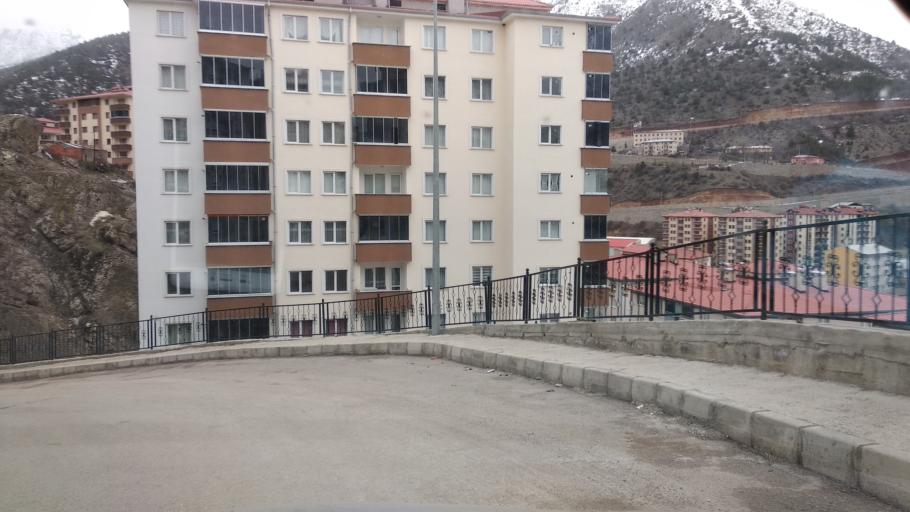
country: TR
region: Gumushane
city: Gumushkhane
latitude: 40.4643
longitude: 39.4670
